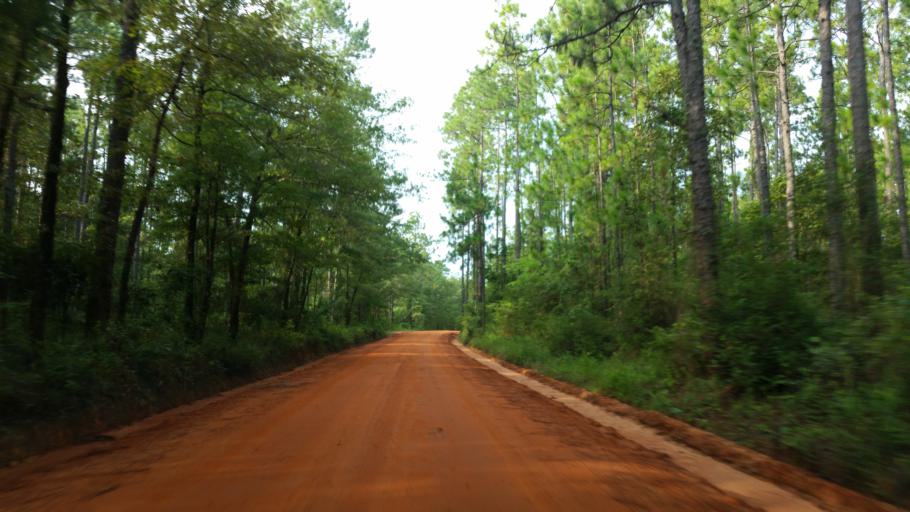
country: US
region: Alabama
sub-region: Escambia County
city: Atmore
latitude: 30.9231
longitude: -87.5755
